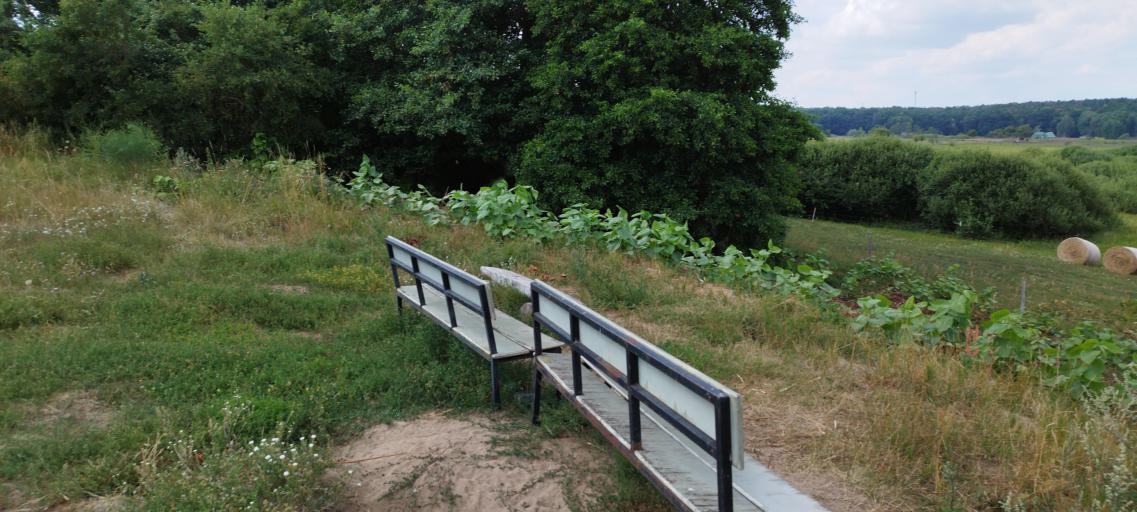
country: DE
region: Brandenburg
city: Rehfelde
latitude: 52.5164
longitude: 13.8554
